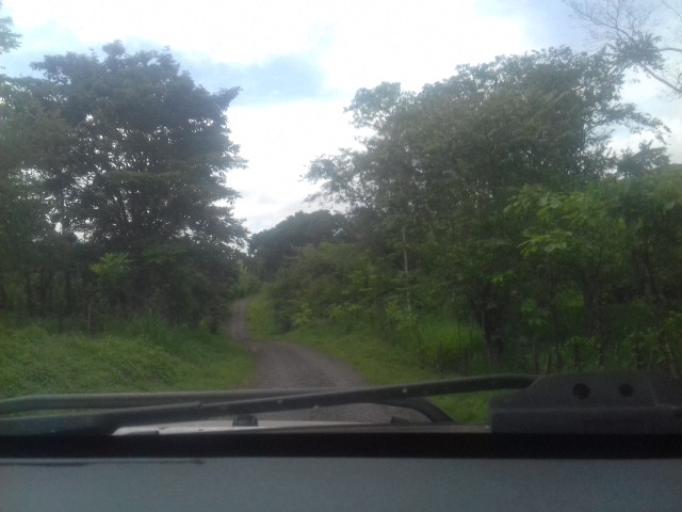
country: NI
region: Atlantico Norte (RAAN)
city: Waslala
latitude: 13.4962
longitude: -85.2313
